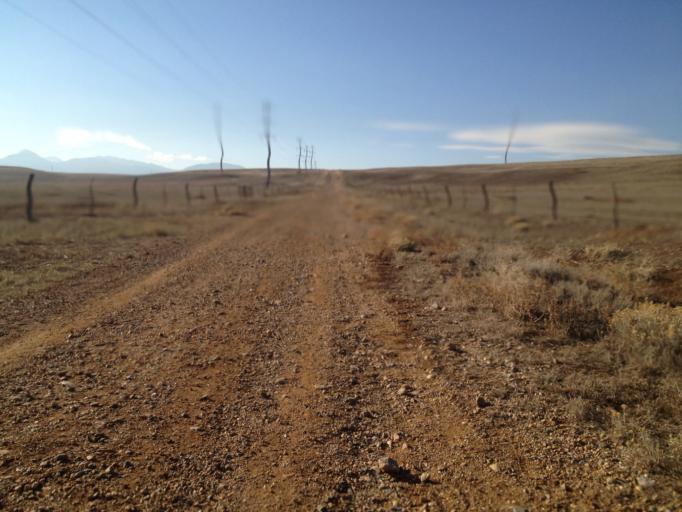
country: US
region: Colorado
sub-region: Boulder County
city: Superior
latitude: 39.9287
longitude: -105.1791
